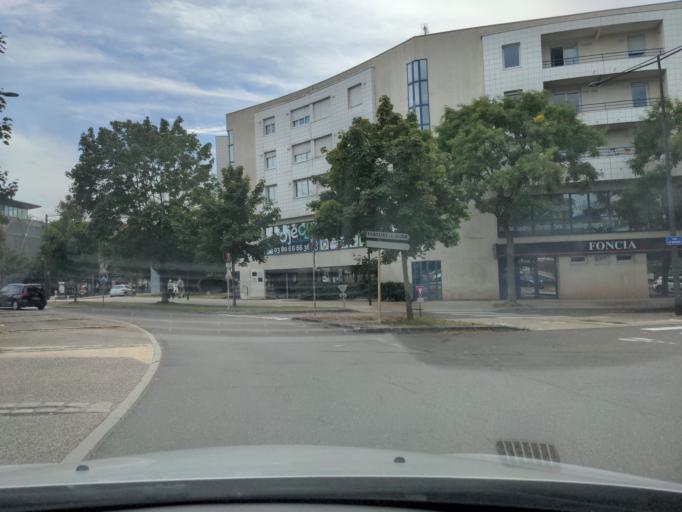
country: FR
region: Bourgogne
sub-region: Departement de la Cote-d'Or
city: Fontaine-les-Dijon
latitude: 47.3472
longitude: 5.0449
